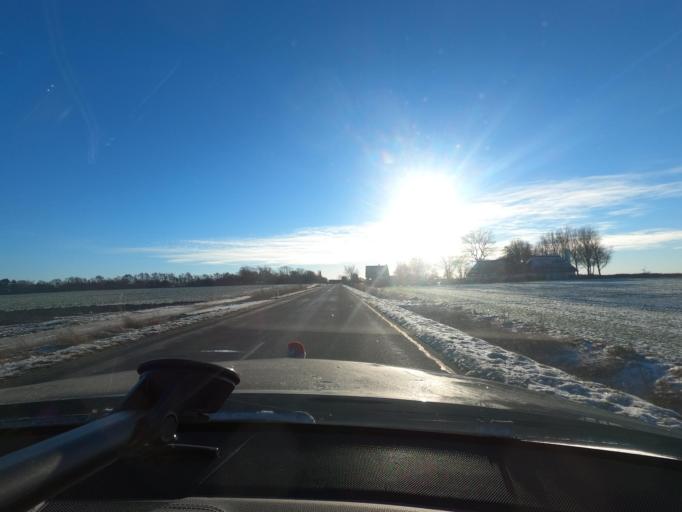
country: DK
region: South Denmark
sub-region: Sonderborg Kommune
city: Horuphav
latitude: 54.8694
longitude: 9.9962
